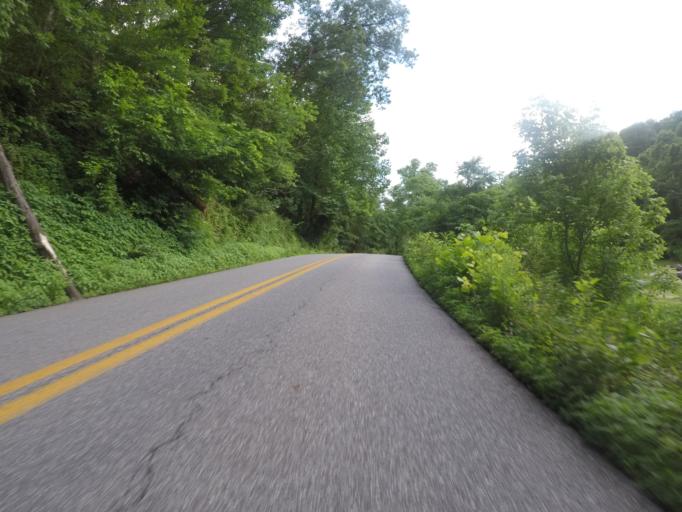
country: US
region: West Virginia
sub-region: Cabell County
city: Pea Ridge
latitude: 38.3966
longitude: -82.3620
